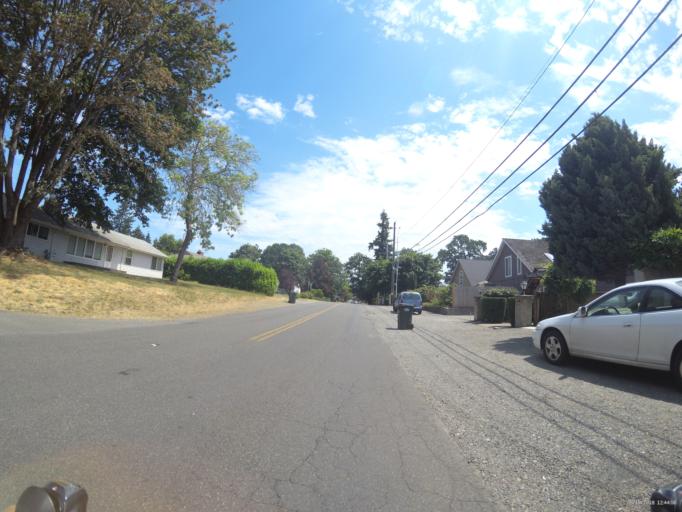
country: US
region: Washington
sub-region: Pierce County
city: Lakewood
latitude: 47.1635
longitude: -122.5232
